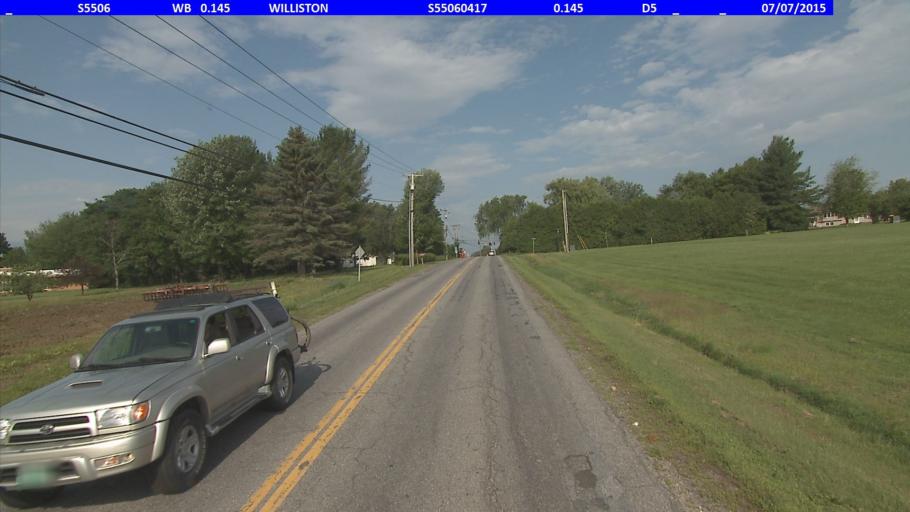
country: US
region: Vermont
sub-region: Chittenden County
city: Essex Junction
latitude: 44.4649
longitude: -73.1100
